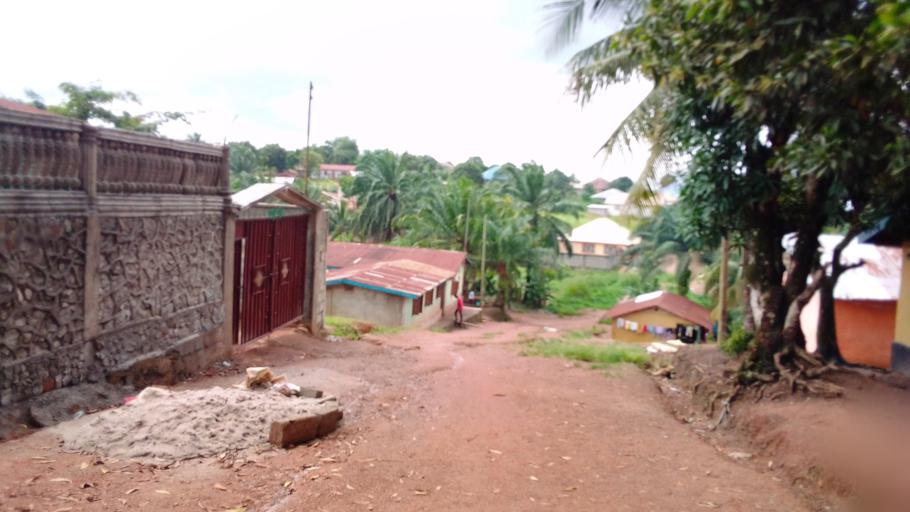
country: SL
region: Eastern Province
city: Kenema
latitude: 7.8723
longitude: -11.1760
